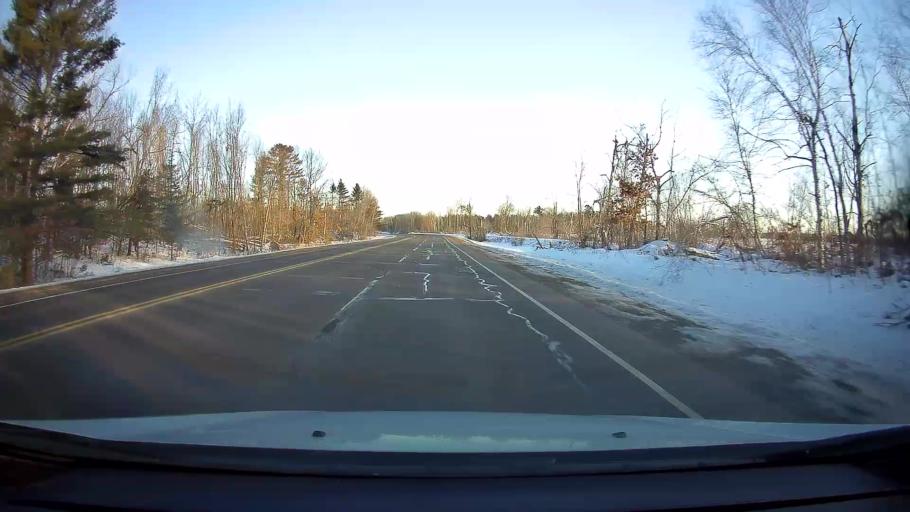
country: US
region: Wisconsin
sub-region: Barron County
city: Turtle Lake
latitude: 45.4279
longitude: -92.1294
